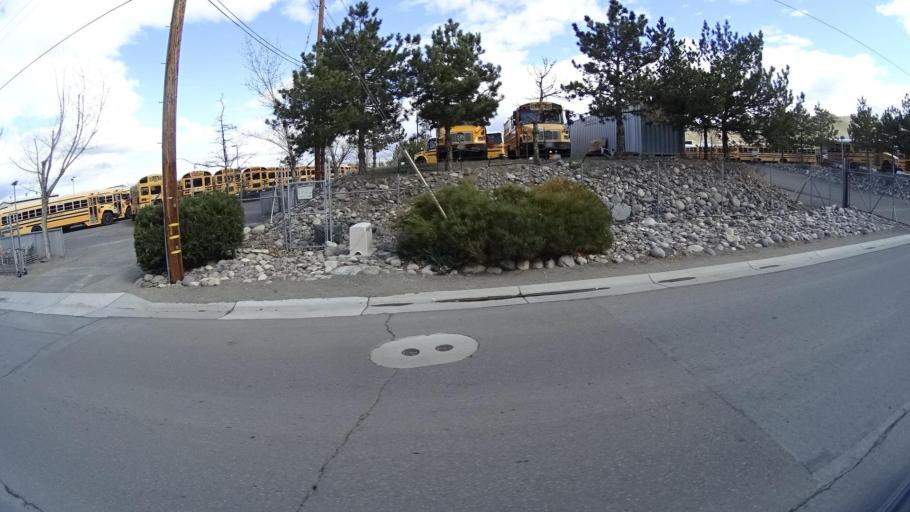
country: US
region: Nevada
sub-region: Washoe County
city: Sparks
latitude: 39.5250
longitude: -119.7074
